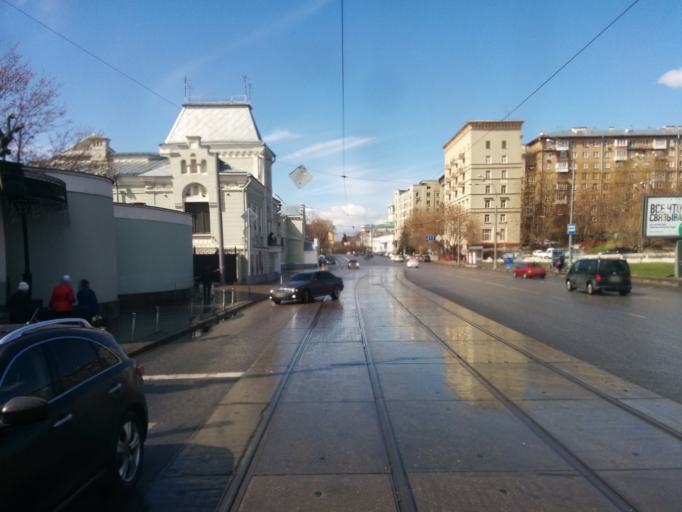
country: RU
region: Moscow
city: Mar'ina Roshcha
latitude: 55.7793
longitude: 37.6221
